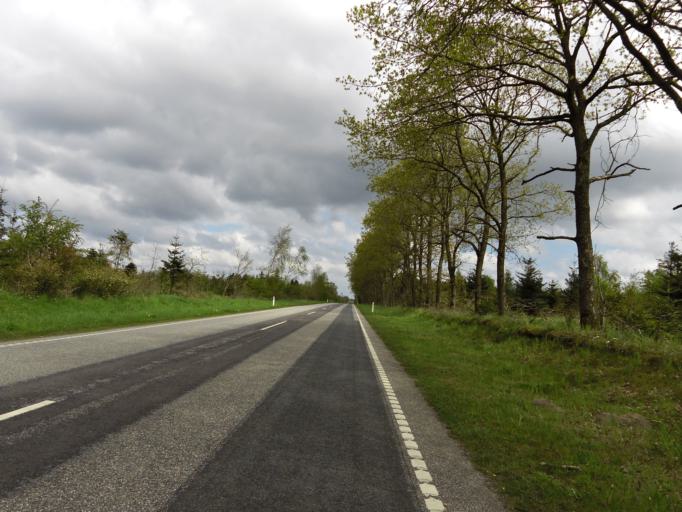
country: DK
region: South Denmark
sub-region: Haderslev Kommune
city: Gram
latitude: 55.2583
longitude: 8.9892
